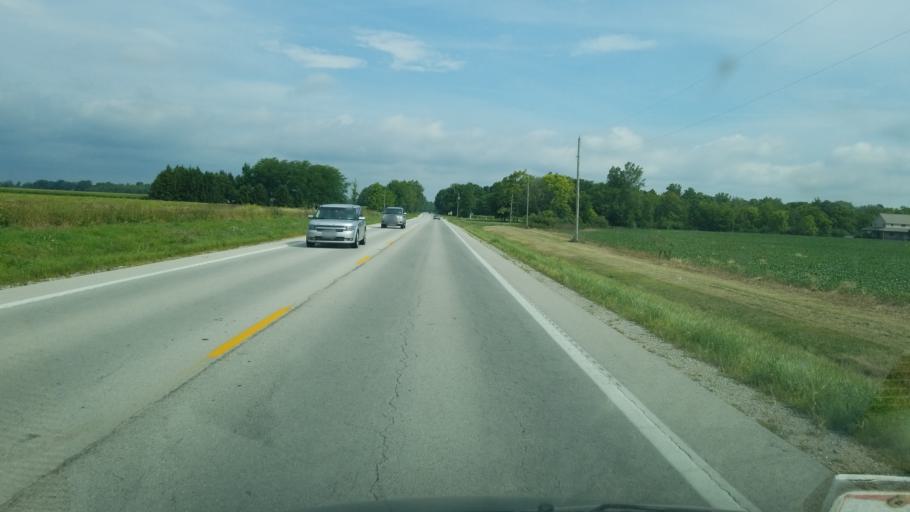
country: US
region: Ohio
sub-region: Sandusky County
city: Ballville
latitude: 41.2606
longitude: -83.1678
